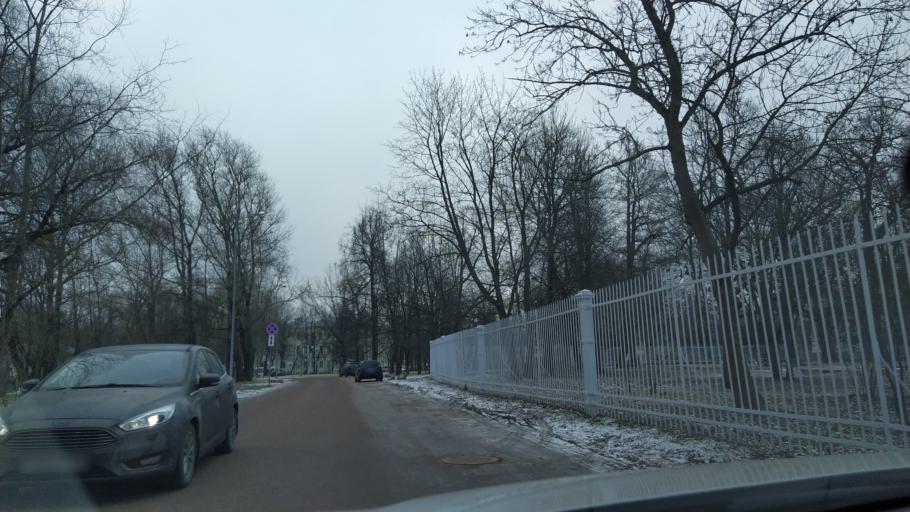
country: RU
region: St.-Petersburg
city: Pushkin
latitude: 59.7231
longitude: 30.3945
